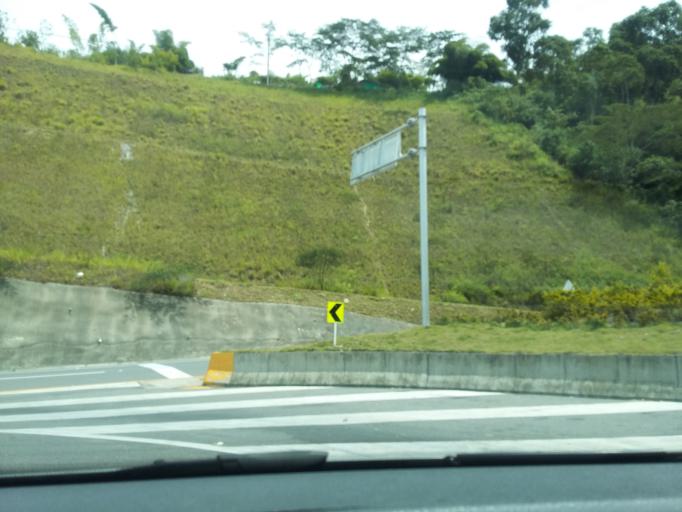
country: CO
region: Santander
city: Bucaramanga
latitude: 7.1119
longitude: -73.0820
